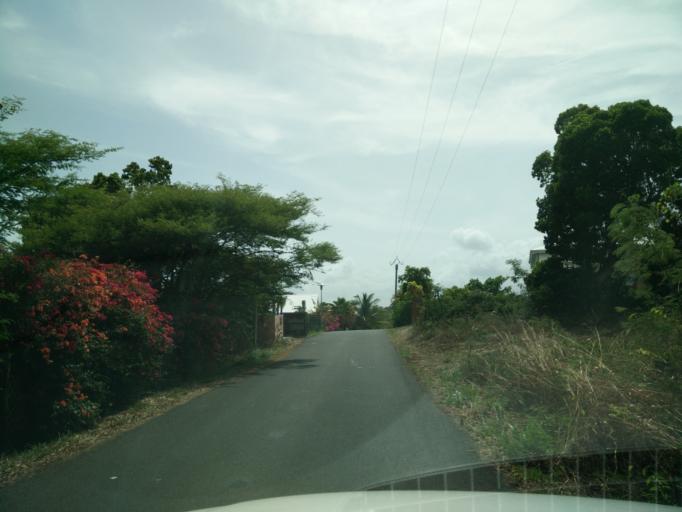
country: GP
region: Guadeloupe
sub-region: Guadeloupe
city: Sainte-Anne
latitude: 16.2432
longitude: -61.3348
